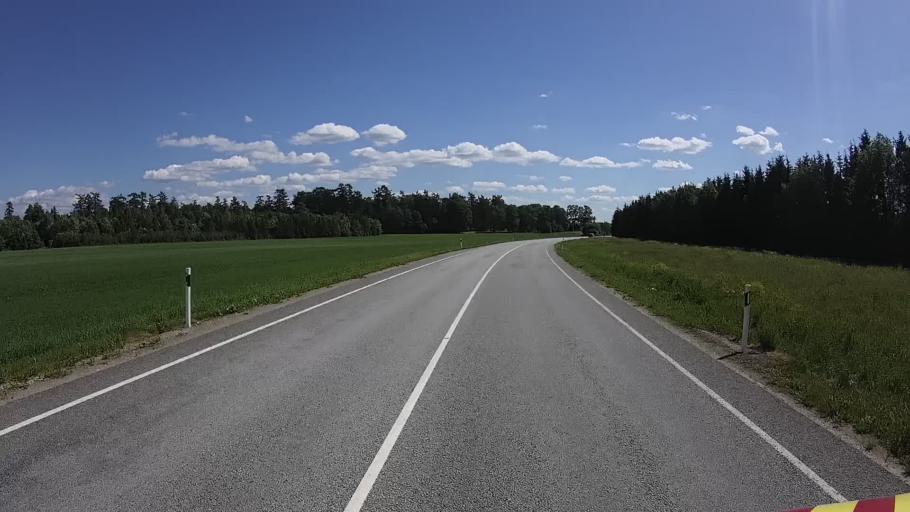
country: EE
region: Ida-Virumaa
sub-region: Johvi vald
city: Johvi
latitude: 59.3800
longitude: 27.3511
